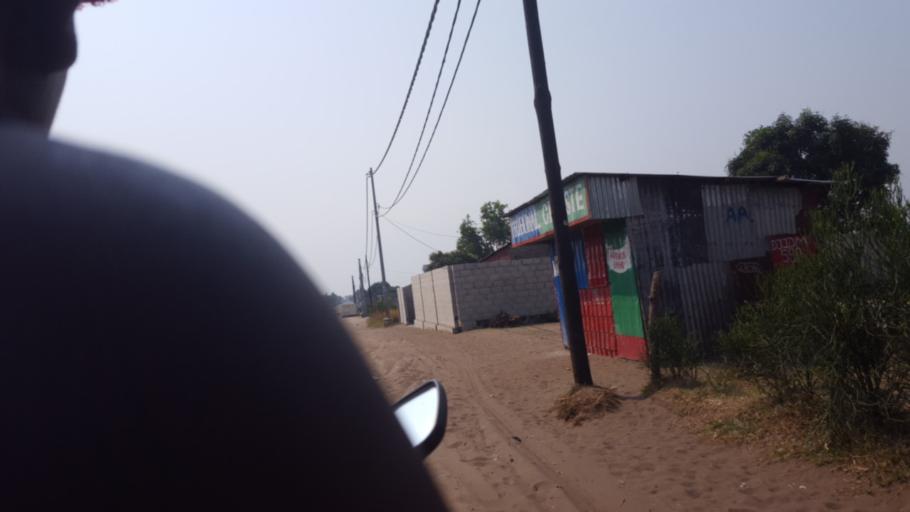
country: CD
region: Kinshasa
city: Masina
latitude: -4.3695
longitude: 15.5155
